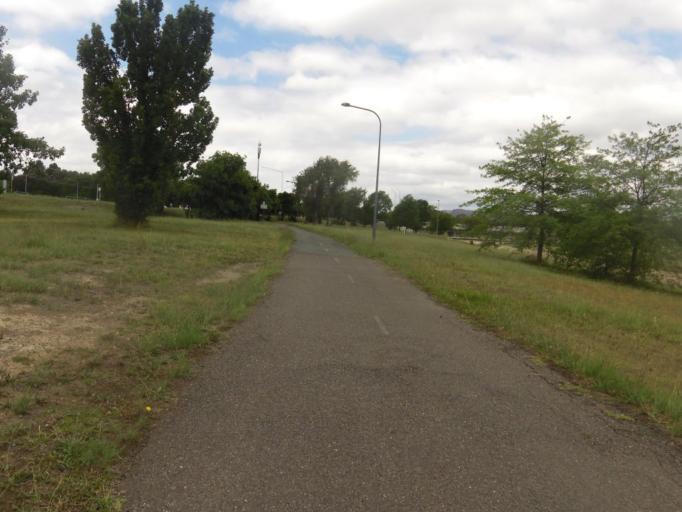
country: AU
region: Australian Capital Territory
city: Macarthur
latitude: -35.4216
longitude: 149.1014
